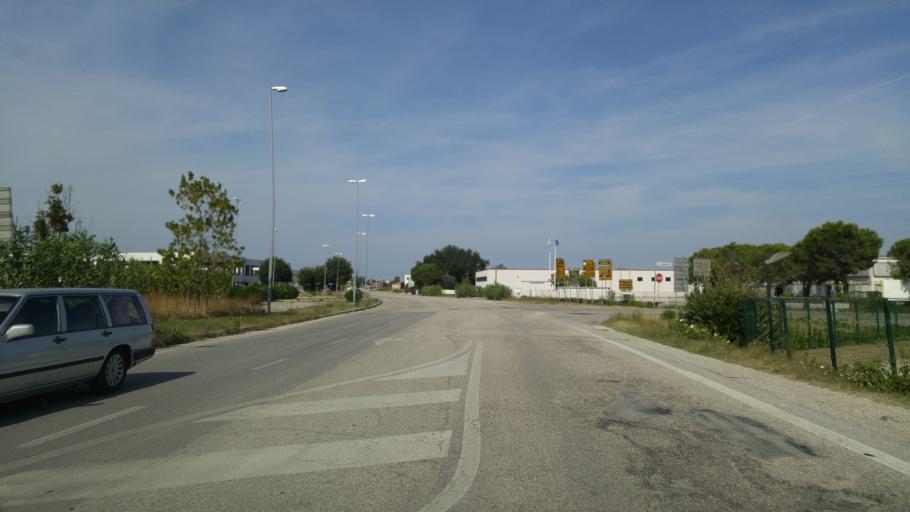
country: IT
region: The Marches
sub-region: Provincia di Pesaro e Urbino
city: Bellocchi
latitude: 43.7884
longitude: 12.9990
